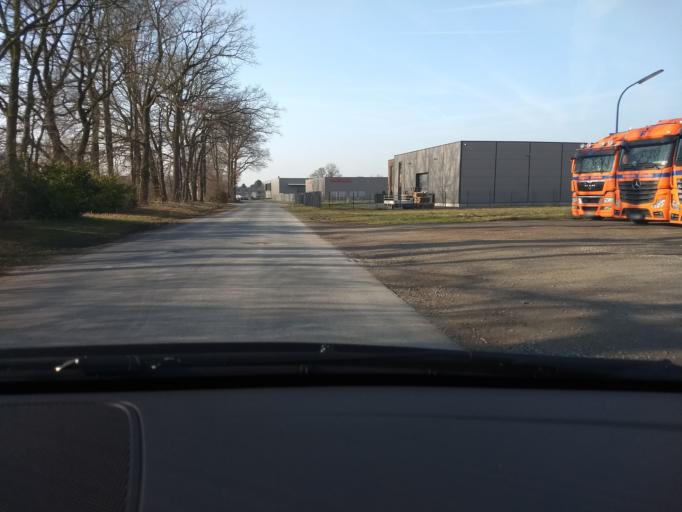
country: DE
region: North Rhine-Westphalia
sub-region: Regierungsbezirk Munster
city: Rhede
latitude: 51.8348
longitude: 6.7209
